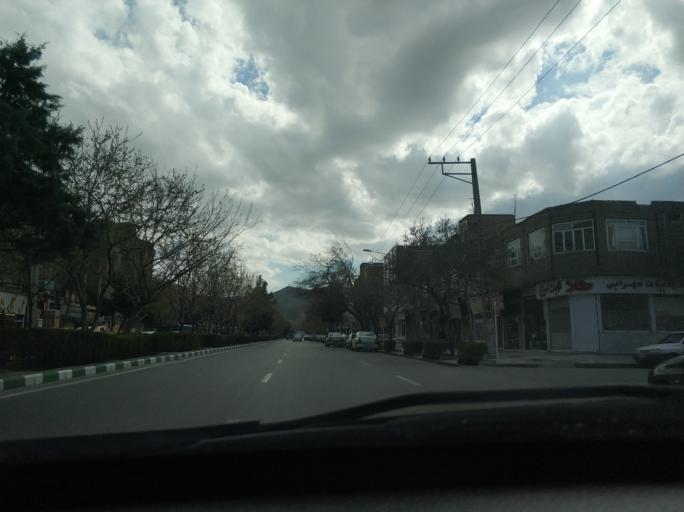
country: IR
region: Razavi Khorasan
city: Mashhad
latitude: 36.2707
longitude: 59.5892
